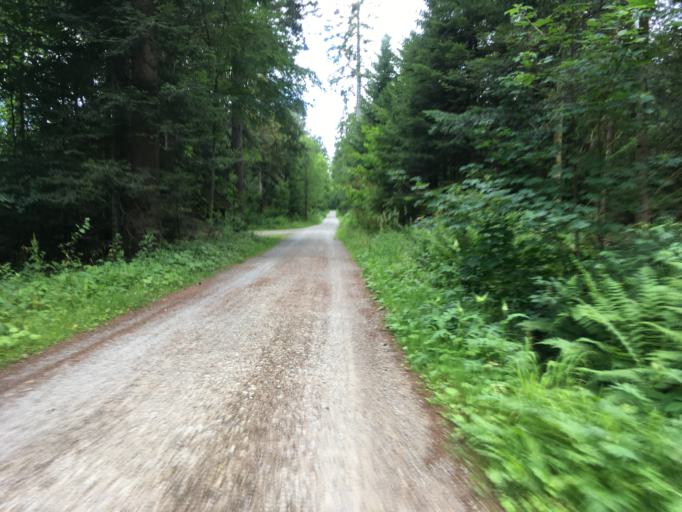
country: DE
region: Baden-Wuerttemberg
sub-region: Karlsruhe Region
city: Freudenstadt
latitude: 48.4469
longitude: 8.4083
